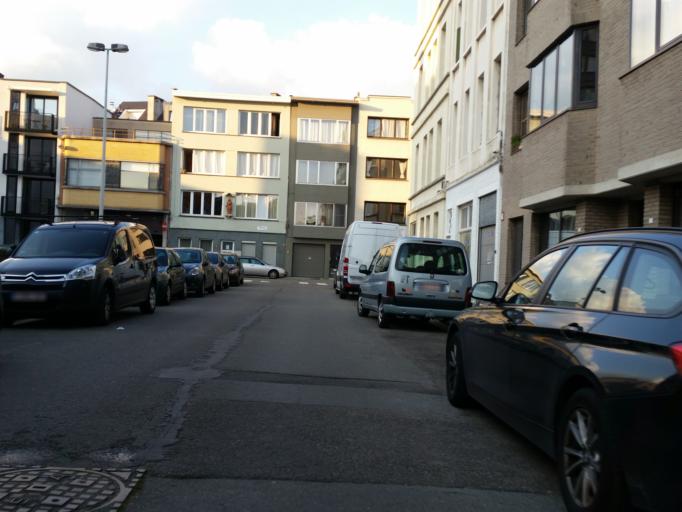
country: BE
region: Flanders
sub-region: Provincie Antwerpen
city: Antwerpen
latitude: 51.2136
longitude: 4.3970
